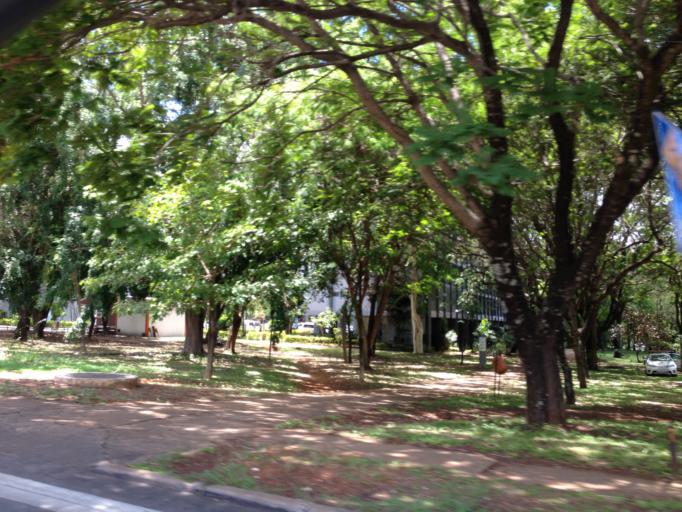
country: BR
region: Federal District
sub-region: Brasilia
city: Brasilia
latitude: -15.8183
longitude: -47.9085
